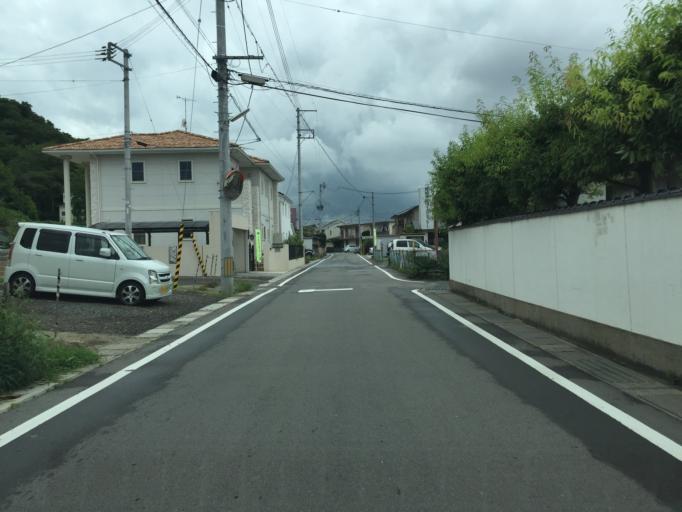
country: JP
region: Fukushima
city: Fukushima-shi
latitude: 37.7440
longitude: 140.4761
